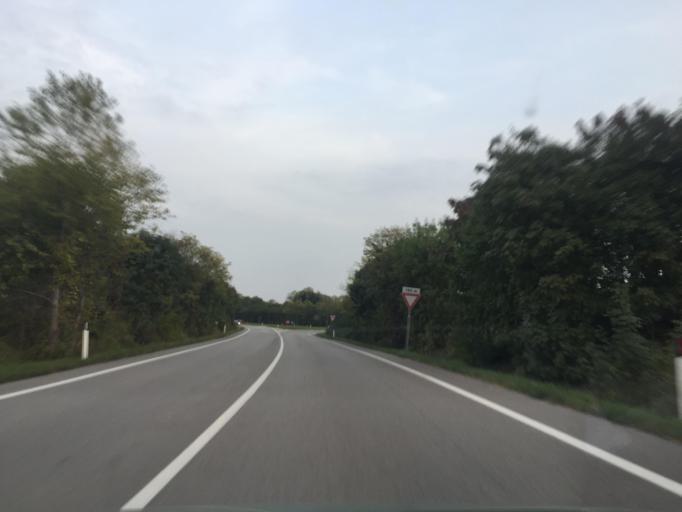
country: IT
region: Friuli Venezia Giulia
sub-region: Provincia di Pordenone
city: Montereale Valcellina
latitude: 46.1473
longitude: 12.6671
